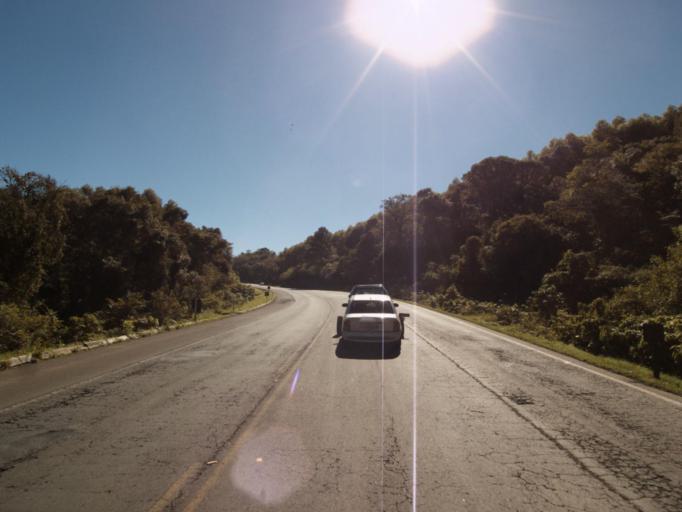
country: BR
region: Rio Grande do Sul
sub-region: Frederico Westphalen
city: Frederico Westphalen
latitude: -26.8413
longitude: -53.1718
